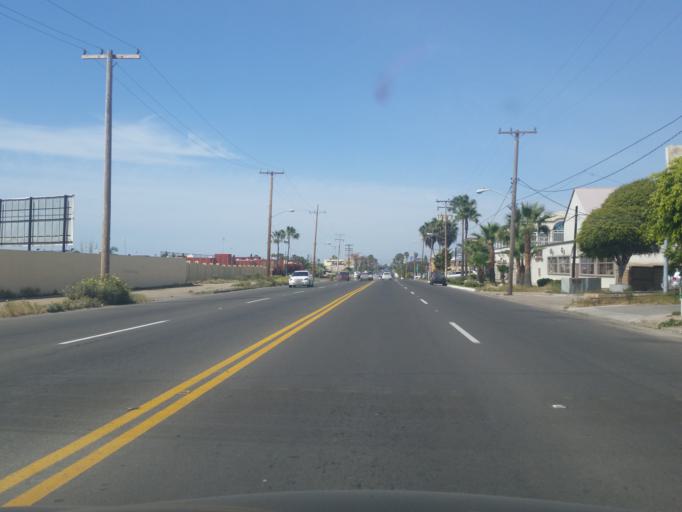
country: MX
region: Baja California
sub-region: Tijuana
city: La Esperanza [Granjas Familiares]
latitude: 32.5168
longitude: -117.1200
